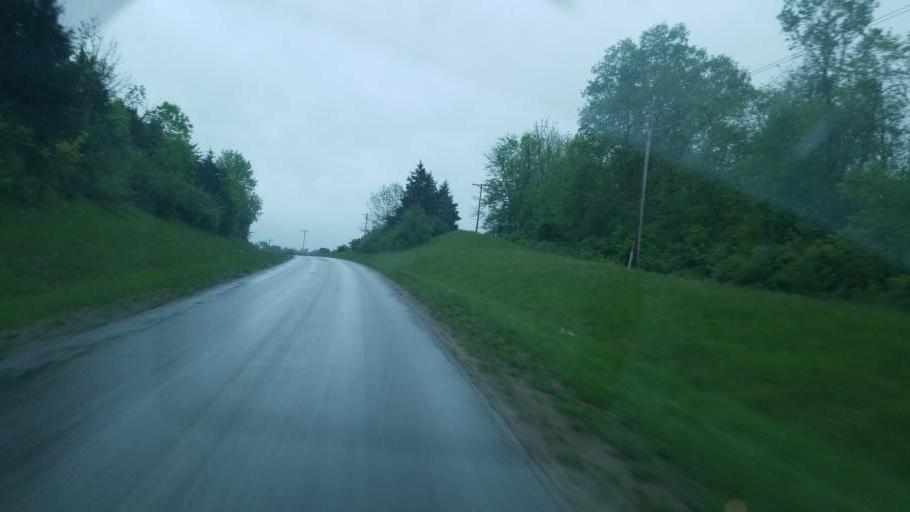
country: US
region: Ohio
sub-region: Highland County
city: Greenfield
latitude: 39.2907
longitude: -83.4612
